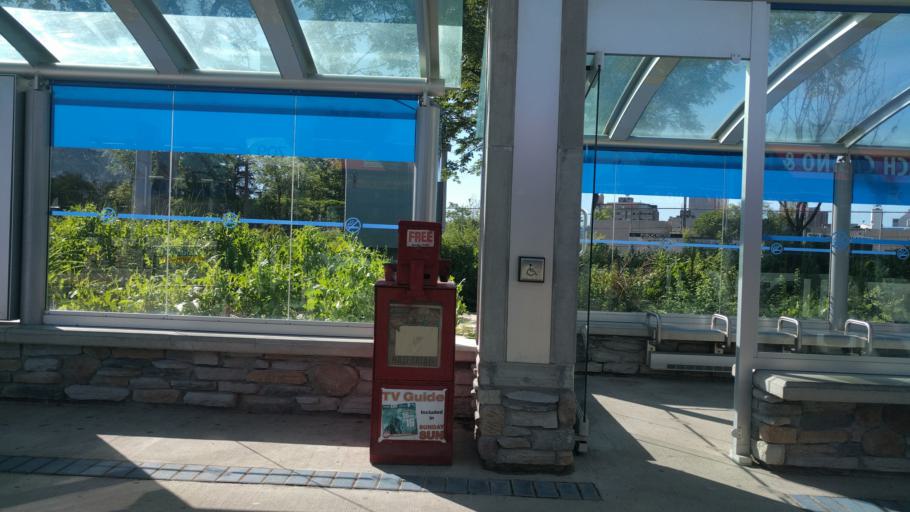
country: CA
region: Manitoba
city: Winnipeg
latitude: 49.8806
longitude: -97.1354
